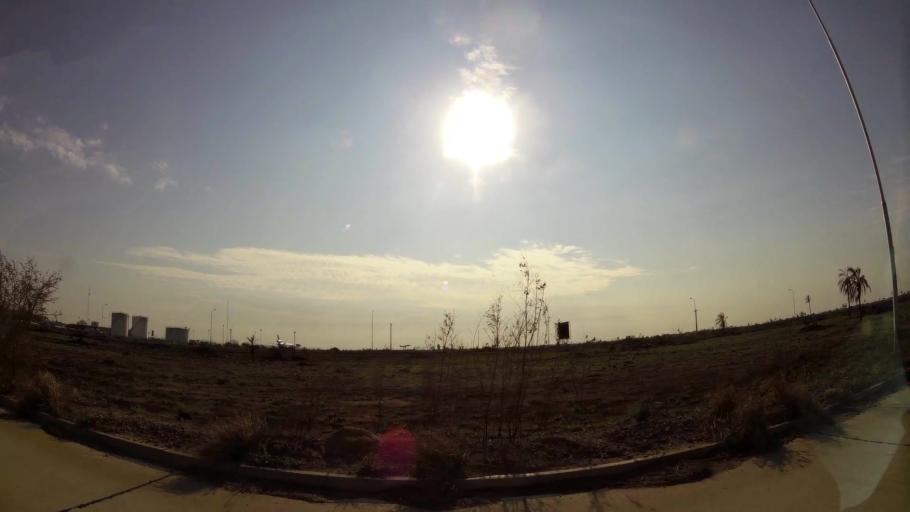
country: BO
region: Santa Cruz
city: Santa Cruz de la Sierra
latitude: -17.6589
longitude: -63.1366
